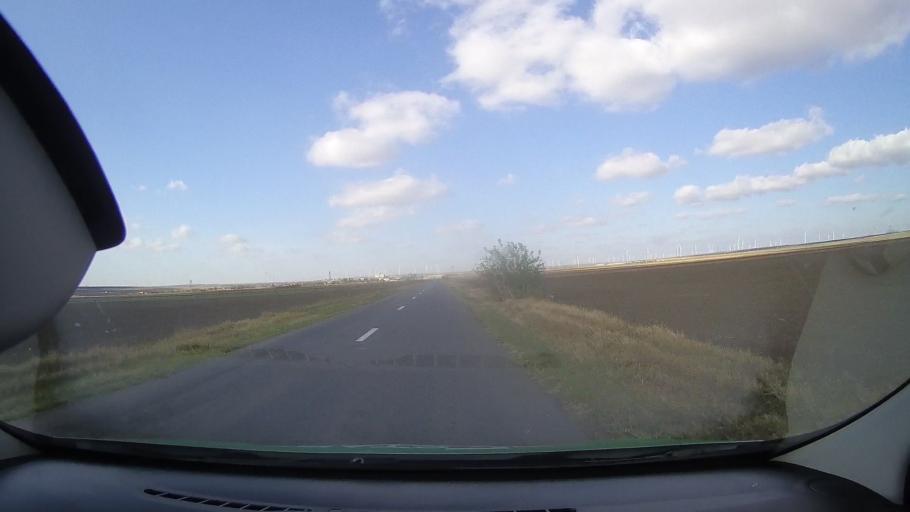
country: RO
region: Constanta
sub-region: Comuna Cogealac
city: Tariverde
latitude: 44.5524
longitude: 28.6244
